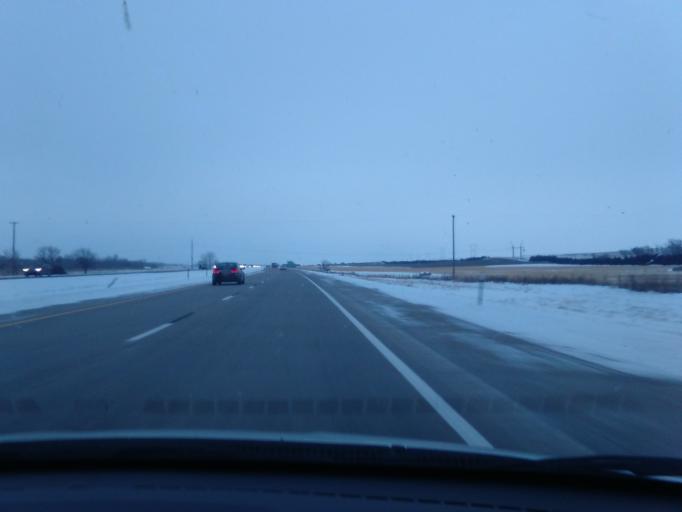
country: US
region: Nebraska
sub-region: Lincoln County
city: Sutherland
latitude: 41.1076
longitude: -101.3859
